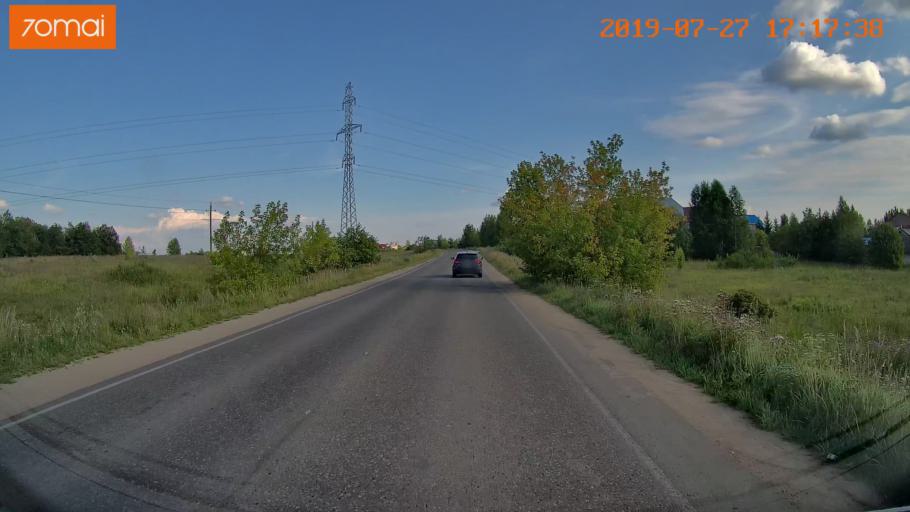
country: RU
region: Ivanovo
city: Novo-Talitsy
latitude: 57.0356
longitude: 40.8968
